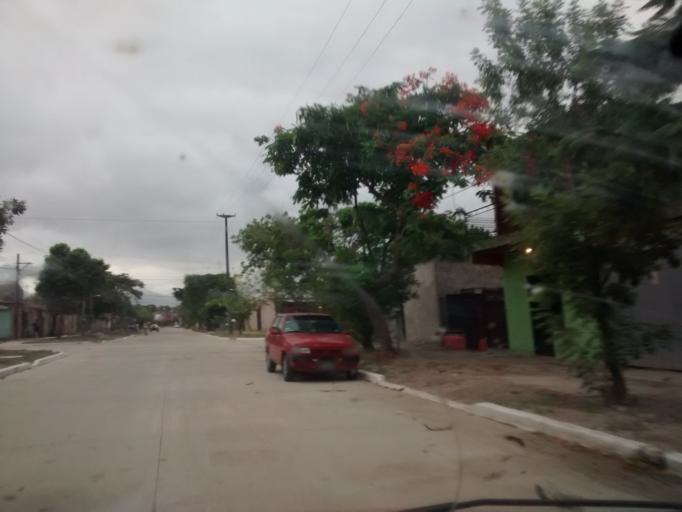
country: AR
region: Chaco
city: Resistencia
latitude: -27.4510
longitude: -59.0109
